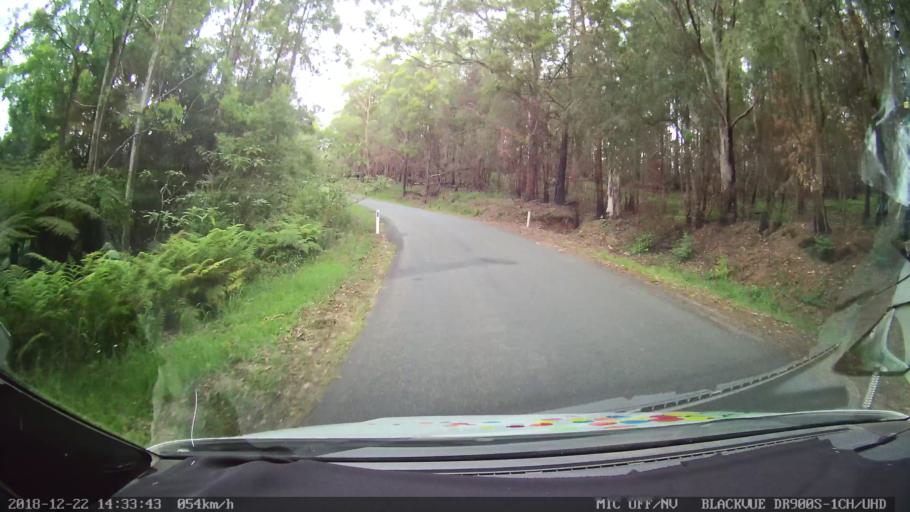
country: AU
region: New South Wales
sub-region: Bellingen
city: Dorrigo
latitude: -30.1147
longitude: 152.6220
